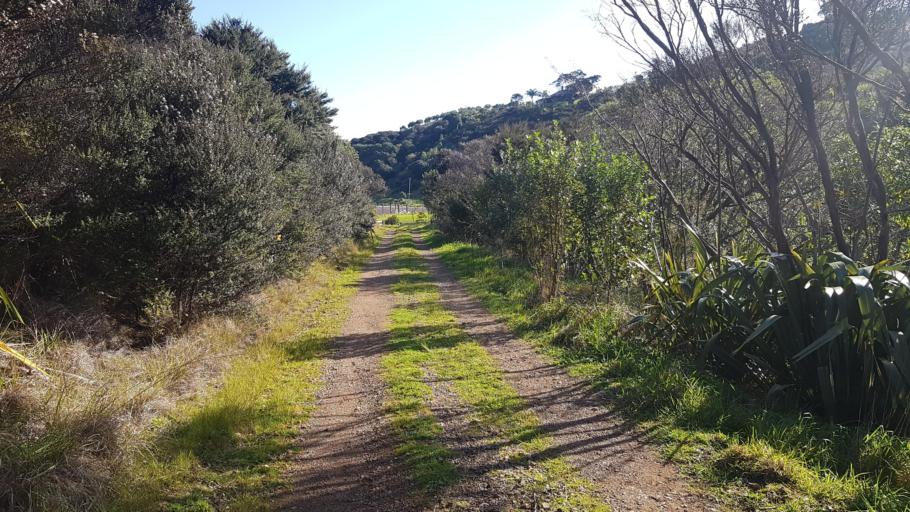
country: NZ
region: Auckland
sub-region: Auckland
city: Pakuranga
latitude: -36.7767
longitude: 174.9919
